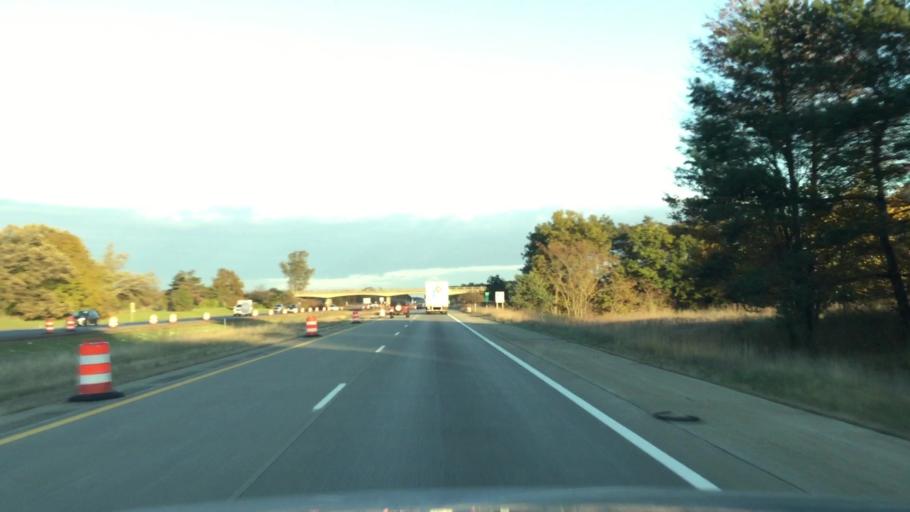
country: US
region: Michigan
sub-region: Calhoun County
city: Marshall
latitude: 42.2825
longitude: -84.9110
